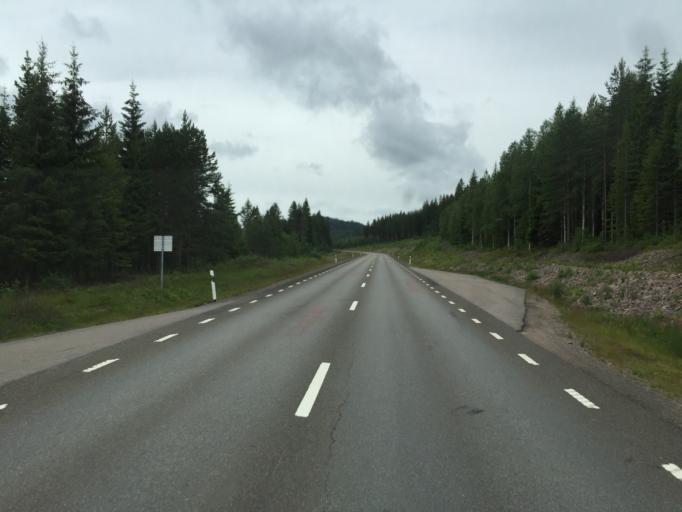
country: SE
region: Dalarna
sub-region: Malung-Saelens kommun
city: Malung
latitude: 60.6249
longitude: 13.6111
